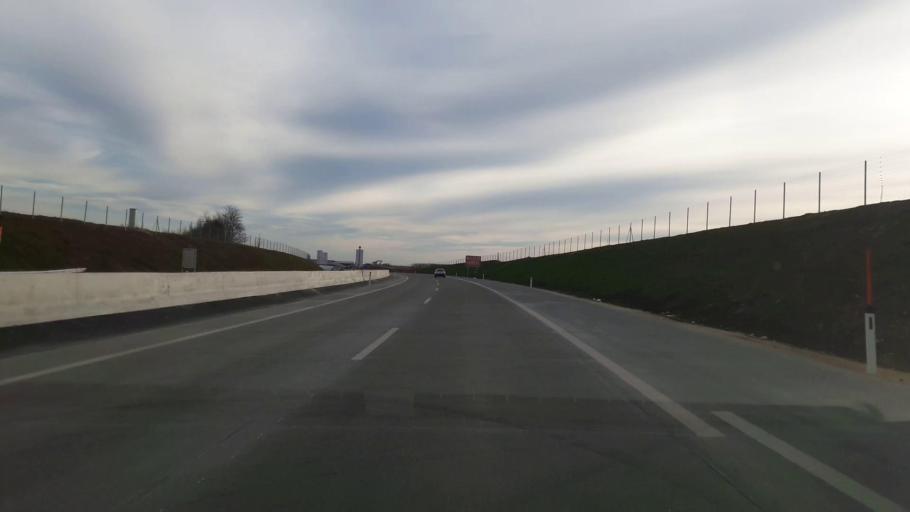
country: AT
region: Lower Austria
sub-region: Politischer Bezirk Mistelbach
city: Herrnbaumgarten
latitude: 48.7008
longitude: 16.6516
